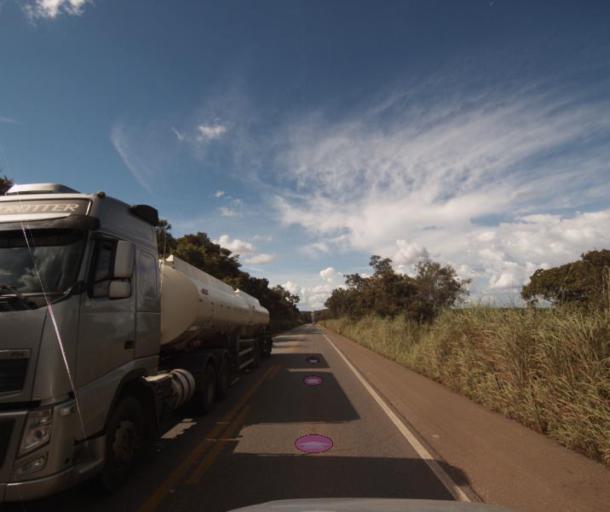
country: BR
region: Goias
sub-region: Porangatu
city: Porangatu
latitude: -13.0982
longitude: -49.1970
